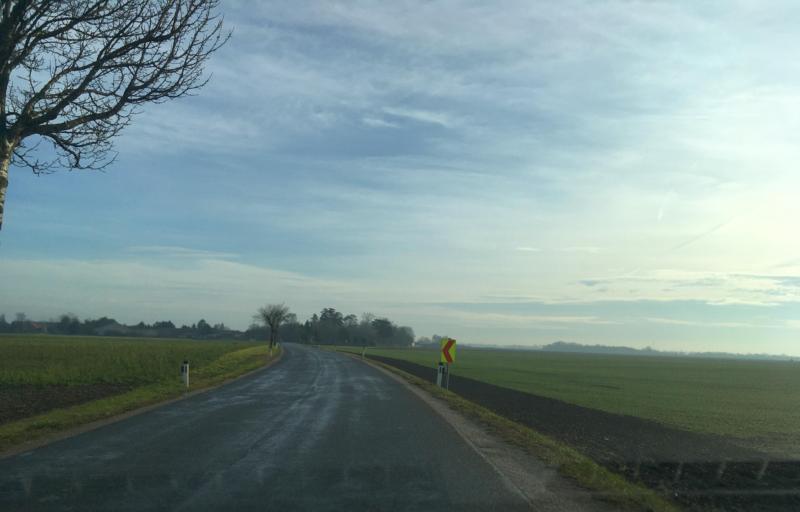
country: AT
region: Lower Austria
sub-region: Politischer Bezirk Ganserndorf
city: Orth an der Donau
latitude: 48.1841
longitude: 16.7306
